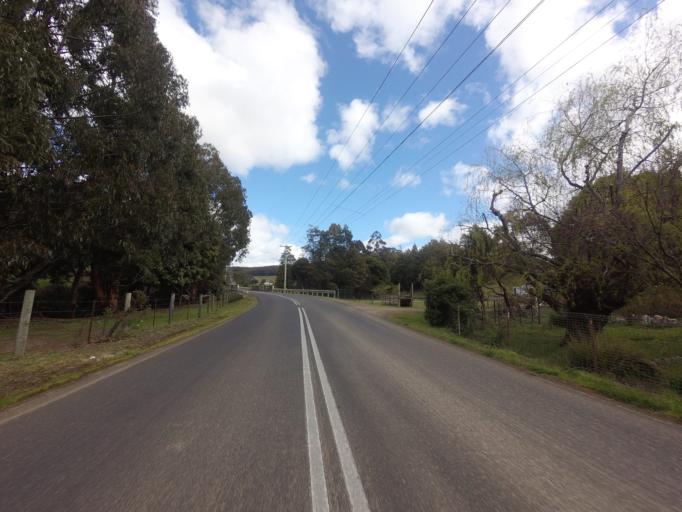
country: AU
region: Tasmania
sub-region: Huon Valley
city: Geeveston
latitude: -43.1754
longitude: 146.9238
